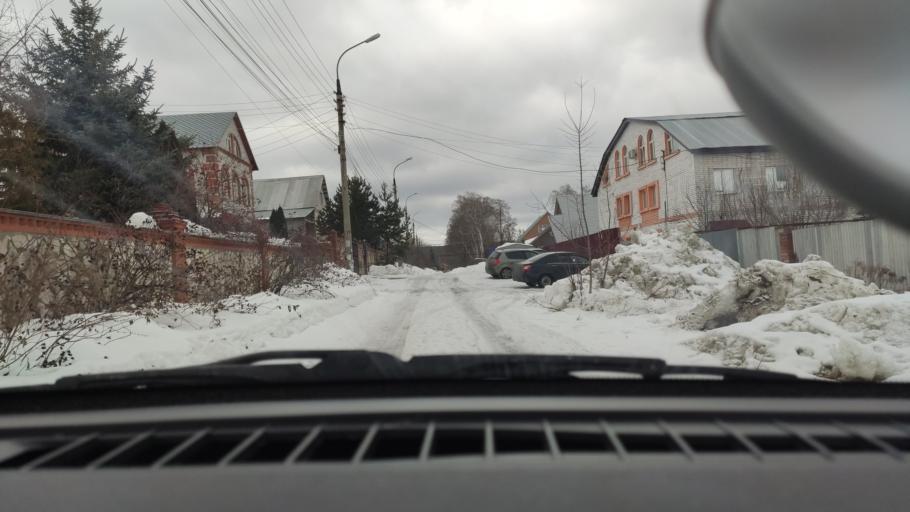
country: RU
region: Samara
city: Petra-Dubrava
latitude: 53.3121
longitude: 50.2881
